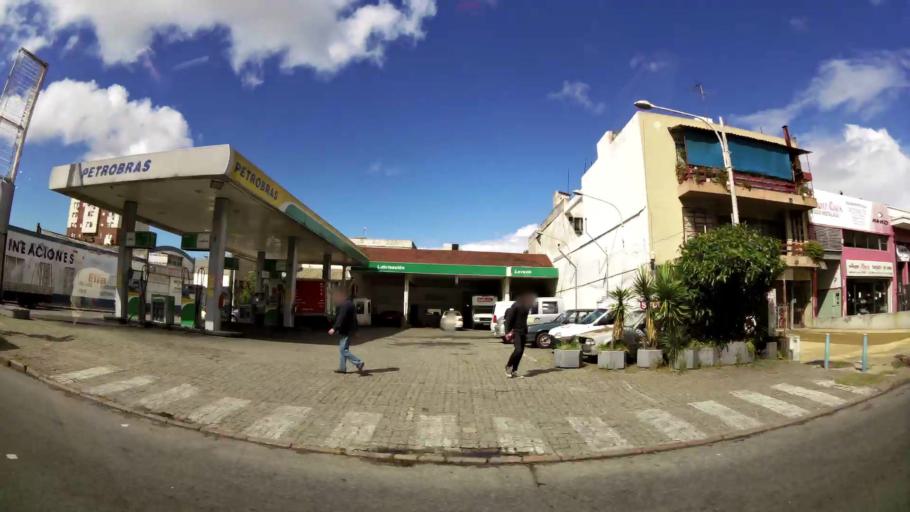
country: UY
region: Montevideo
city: Montevideo
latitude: -34.8834
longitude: -56.1943
